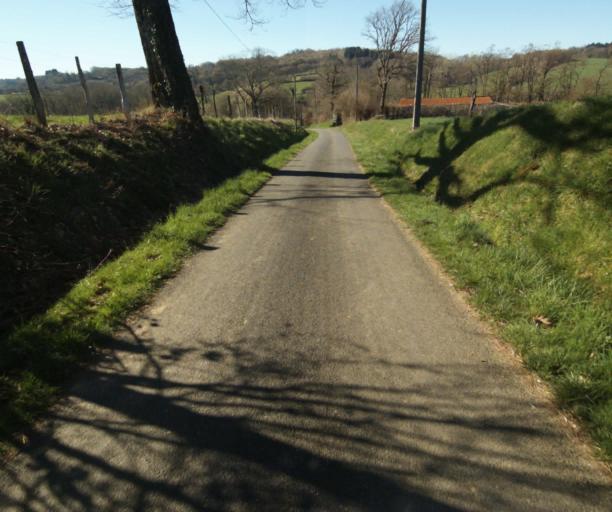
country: FR
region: Limousin
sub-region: Departement de la Correze
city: Chamboulive
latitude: 45.4209
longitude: 1.7093
